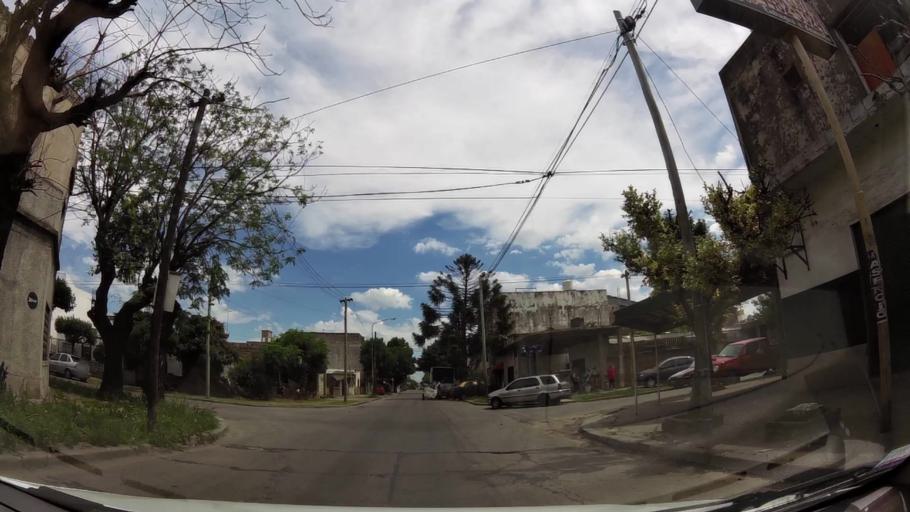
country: AR
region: Buenos Aires
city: San Justo
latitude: -34.6828
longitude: -58.5432
